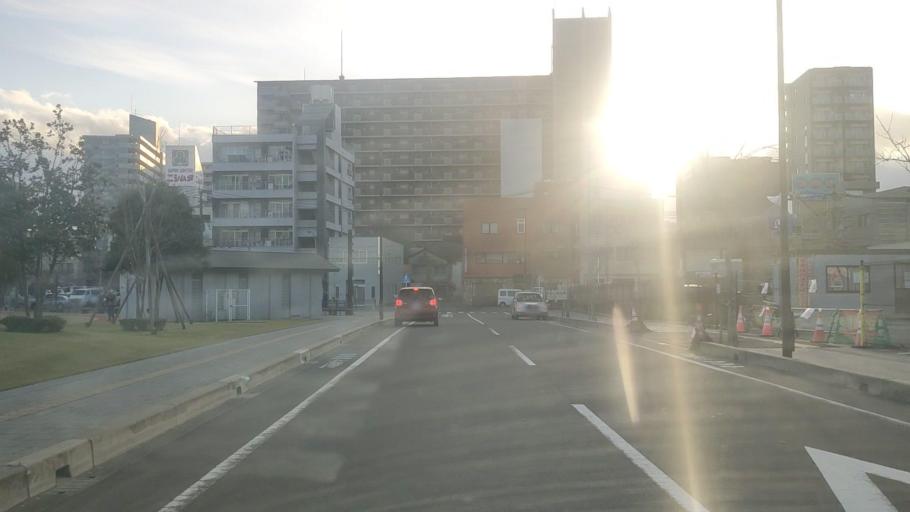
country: JP
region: Kagoshima
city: Kagoshima-shi
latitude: 31.6004
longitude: 130.5629
